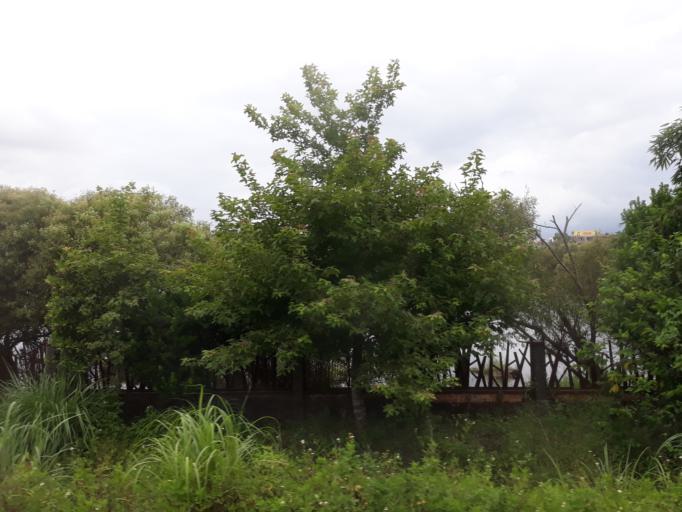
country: TW
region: Taiwan
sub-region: Yilan
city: Yilan
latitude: 24.6852
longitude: 121.7748
